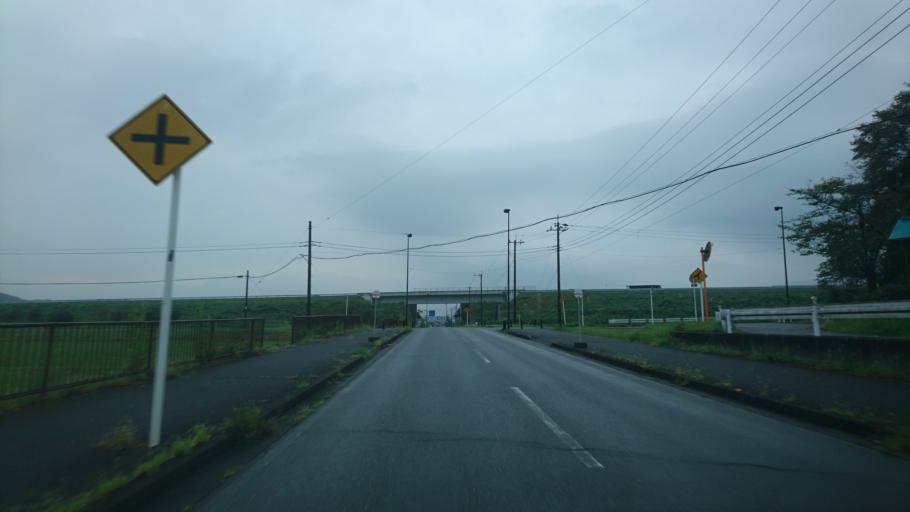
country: JP
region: Chiba
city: Kimitsu
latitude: 35.3050
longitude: 139.9390
